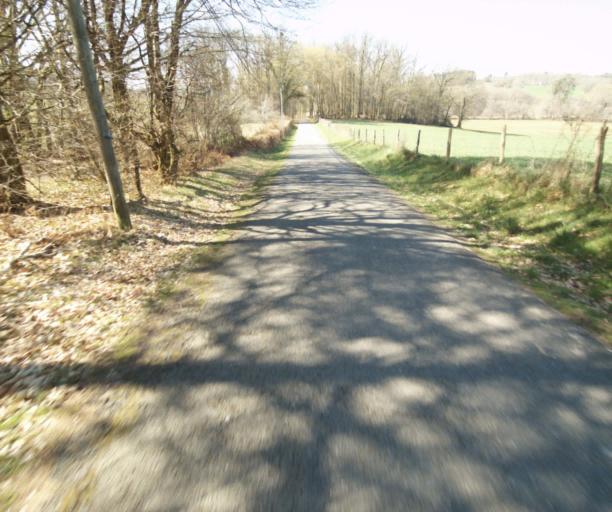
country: FR
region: Limousin
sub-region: Departement de la Correze
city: Saint-Mexant
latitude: 45.3070
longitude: 1.6336
